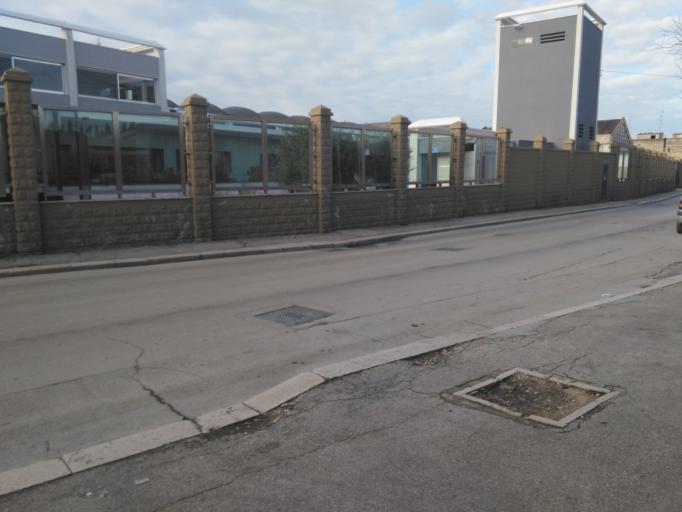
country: IT
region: Apulia
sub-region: Provincia di Barletta - Andria - Trani
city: Andria
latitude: 41.2183
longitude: 16.2966
